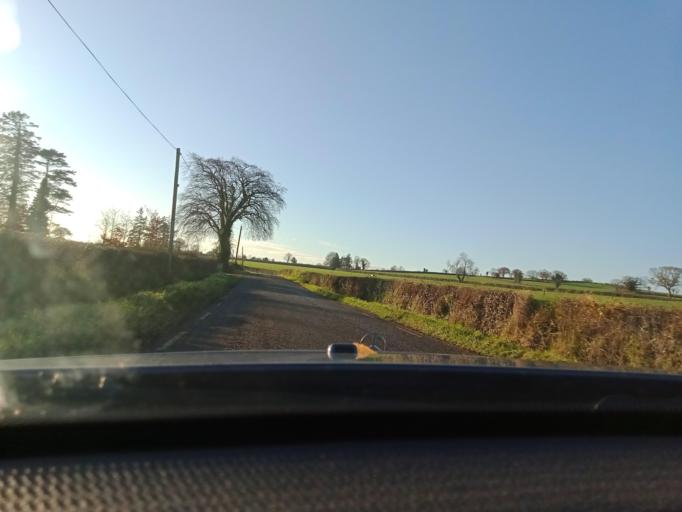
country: IE
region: Leinster
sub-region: Kilkenny
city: Callan
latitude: 52.4978
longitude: -7.3816
